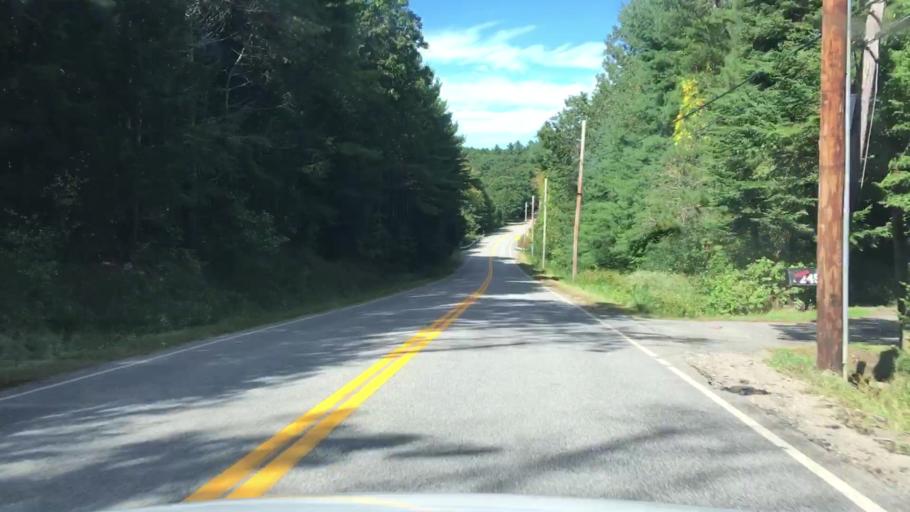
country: US
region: Maine
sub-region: Cumberland County
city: West Scarborough
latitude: 43.6258
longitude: -70.4084
